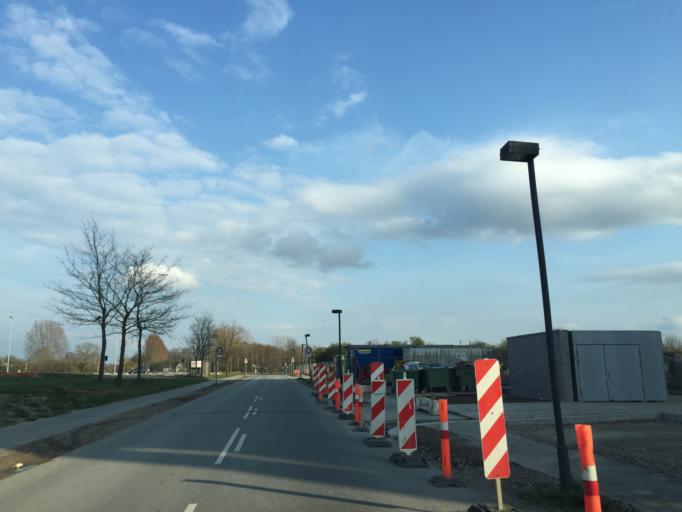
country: DK
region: South Denmark
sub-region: Odense Kommune
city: Neder Holluf
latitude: 55.3736
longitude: 10.4295
